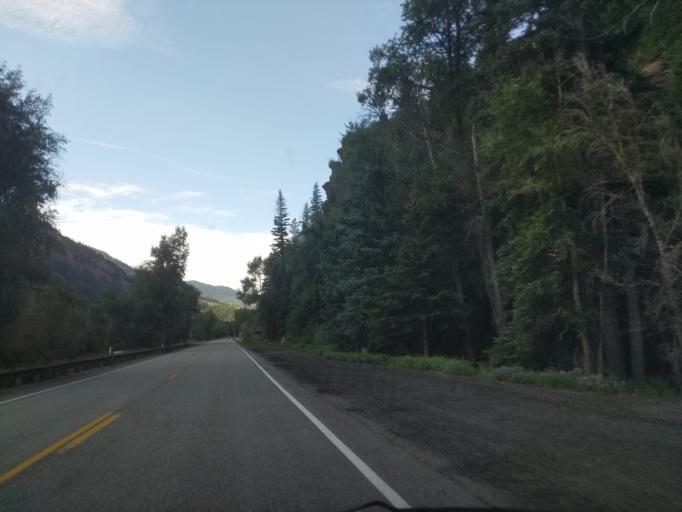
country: US
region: Colorado
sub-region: Garfield County
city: Carbondale
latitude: 39.1983
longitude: -107.2333
